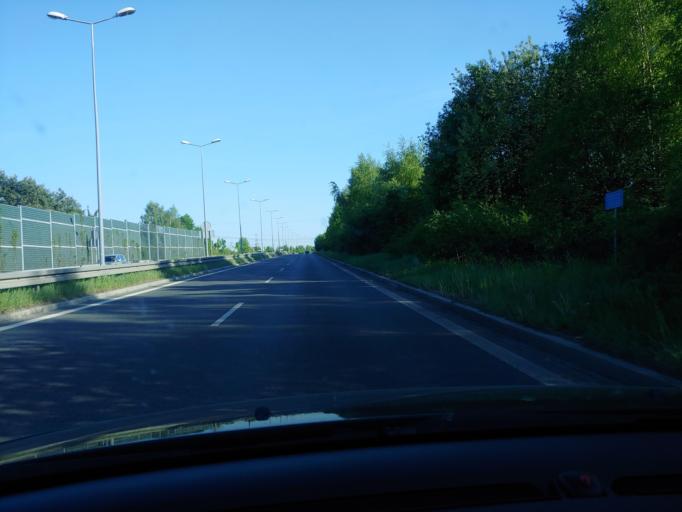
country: PL
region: Silesian Voivodeship
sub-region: Jaworzno
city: Jaworzno
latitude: 50.1796
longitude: 19.2916
